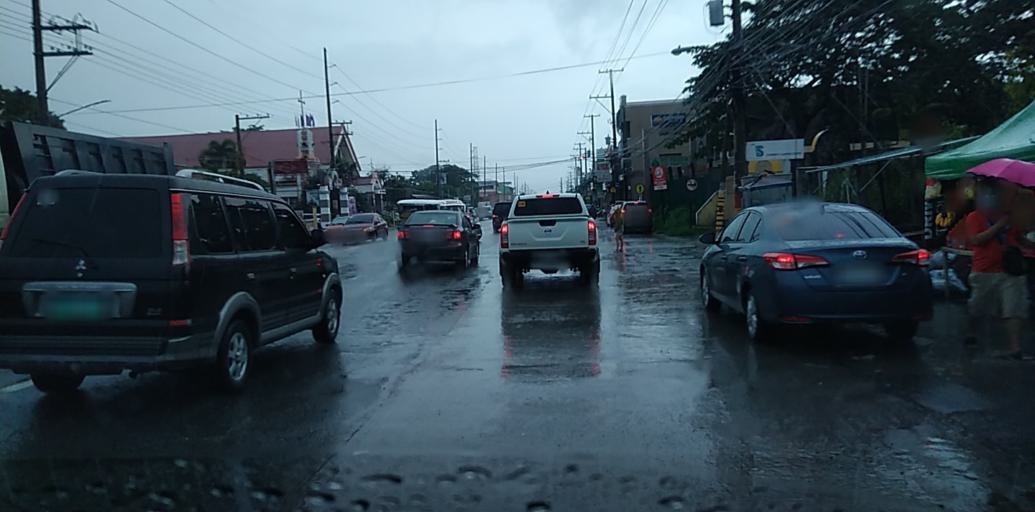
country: PH
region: Central Luzon
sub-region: Province of Pampanga
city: Magliman
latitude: 15.0480
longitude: 120.6678
